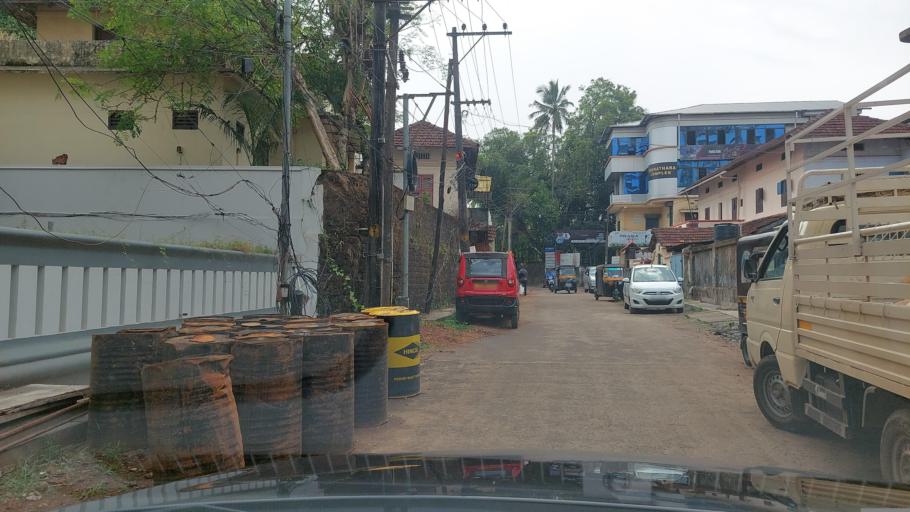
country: IN
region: Kerala
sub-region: Kozhikode
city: Kozhikode
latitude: 11.2470
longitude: 75.7868
